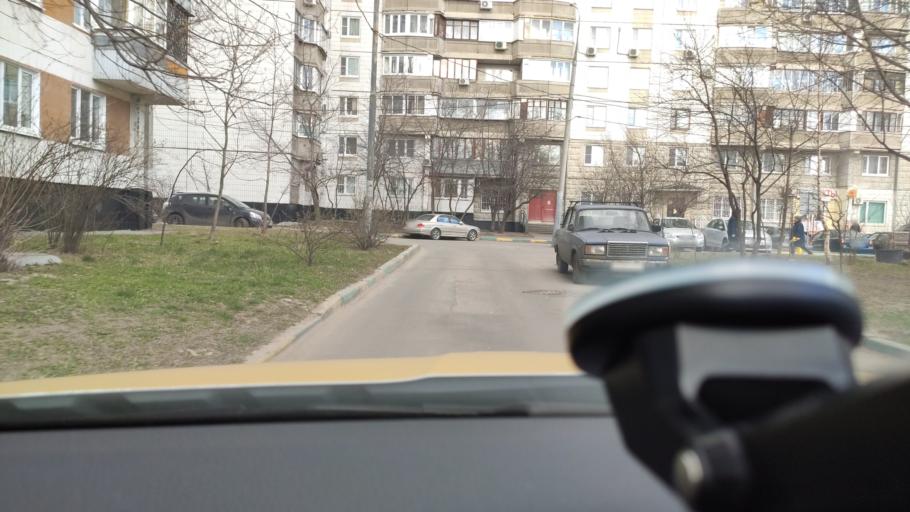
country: RU
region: Moskovskaya
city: Pavshino
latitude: 55.8566
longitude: 37.3510
